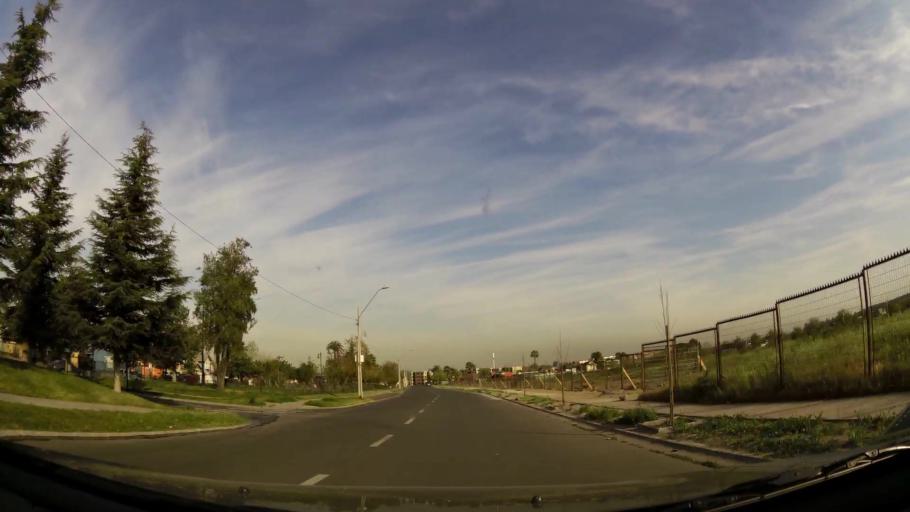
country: CL
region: Santiago Metropolitan
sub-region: Provincia de Cordillera
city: Puente Alto
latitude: -33.5622
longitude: -70.5475
